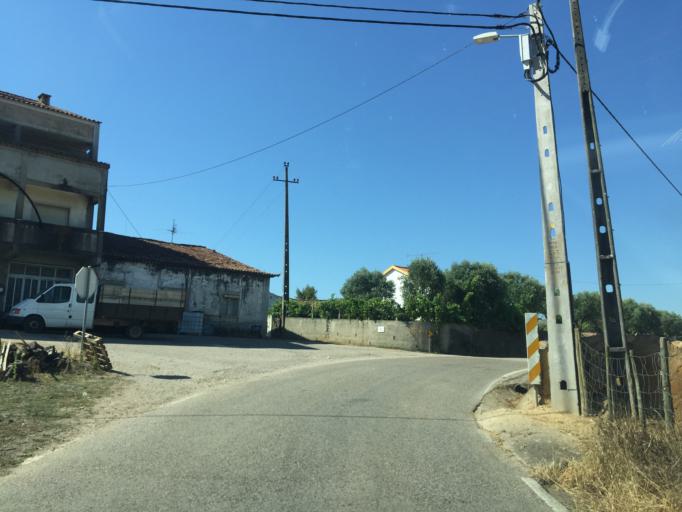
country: PT
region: Santarem
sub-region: Tomar
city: Tomar
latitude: 39.5755
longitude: -8.3255
